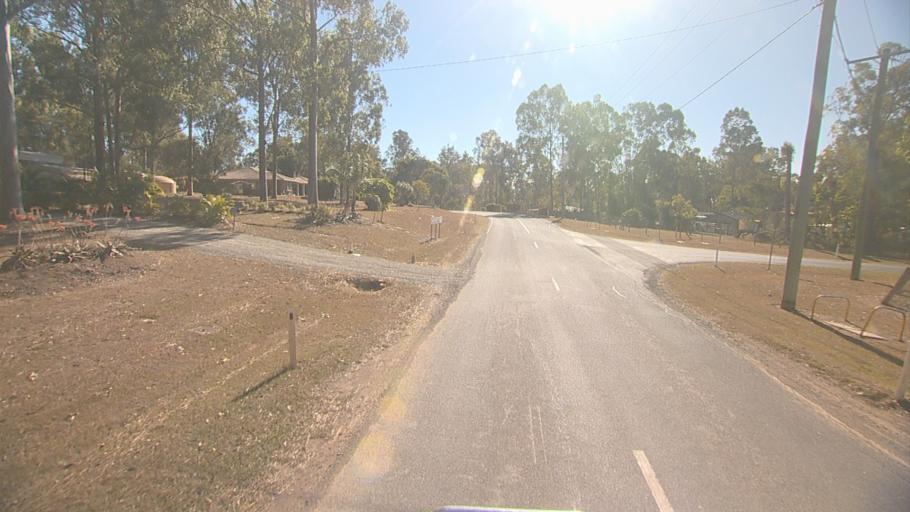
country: AU
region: Queensland
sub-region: Logan
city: Cedar Vale
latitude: -27.8811
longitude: 152.9967
